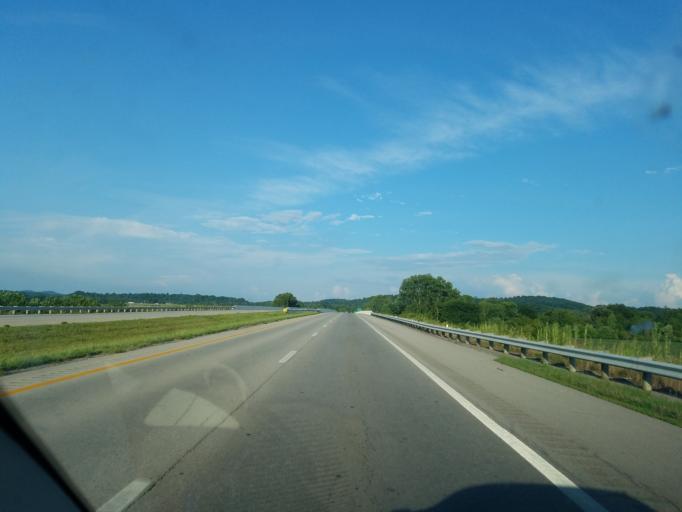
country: US
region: Ohio
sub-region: Pike County
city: Piketon
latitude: 39.0464
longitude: -83.0416
